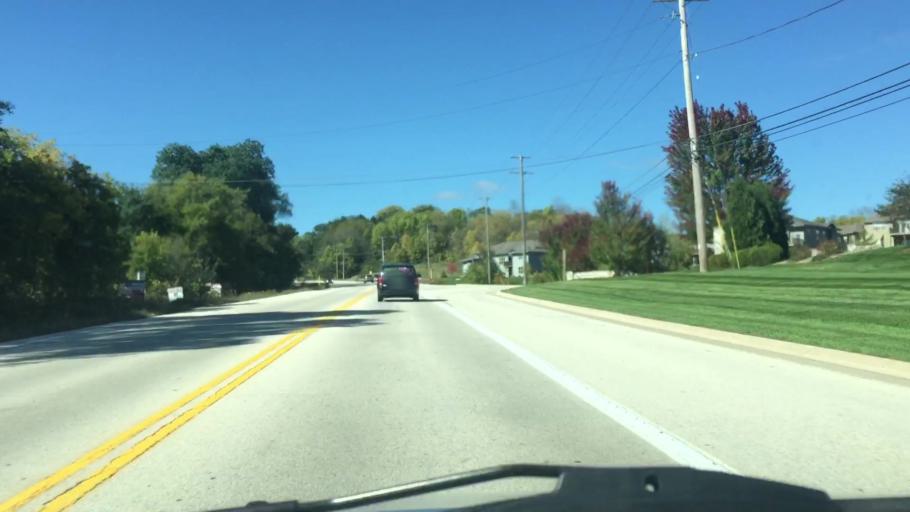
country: US
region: Wisconsin
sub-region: Waukesha County
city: Waukesha
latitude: 43.0218
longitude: -88.2930
